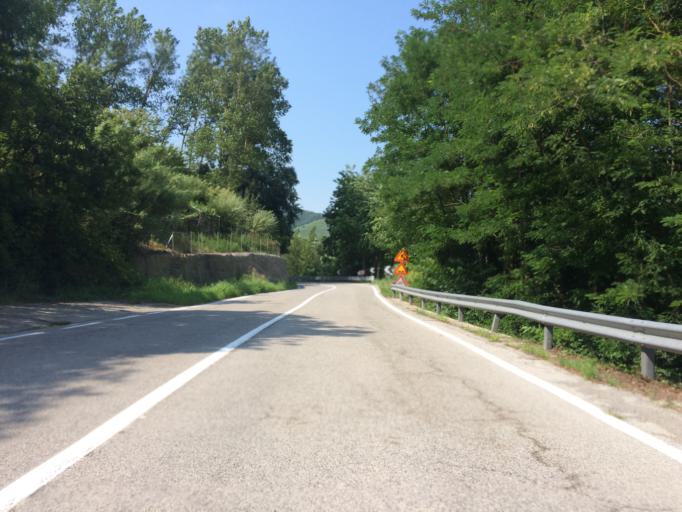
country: IT
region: Piedmont
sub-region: Provincia di Cuneo
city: Torre Bormida
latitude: 44.5705
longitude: 8.1701
